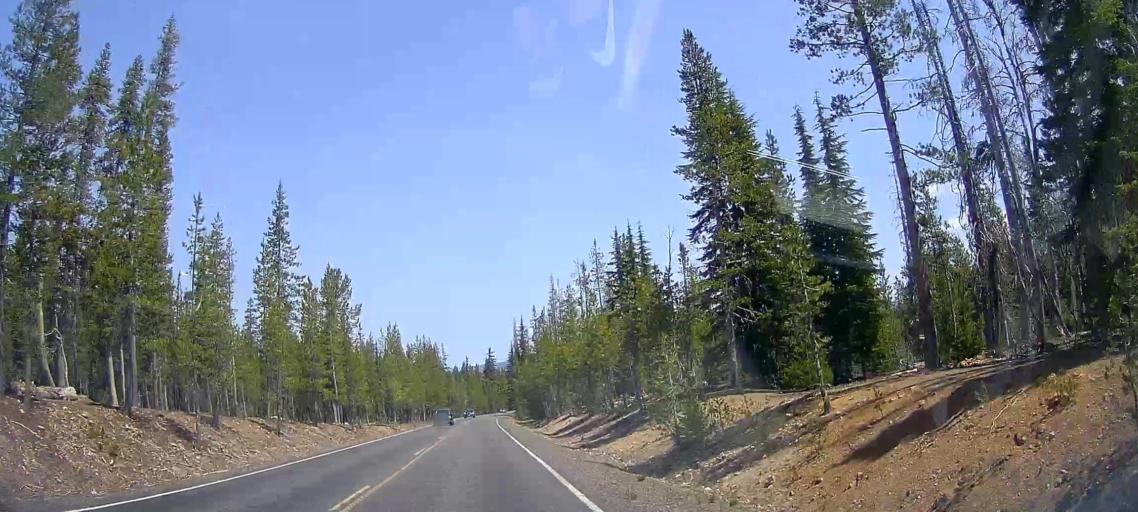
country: US
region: Oregon
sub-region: Jackson County
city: Shady Cove
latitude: 43.0032
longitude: -122.1341
